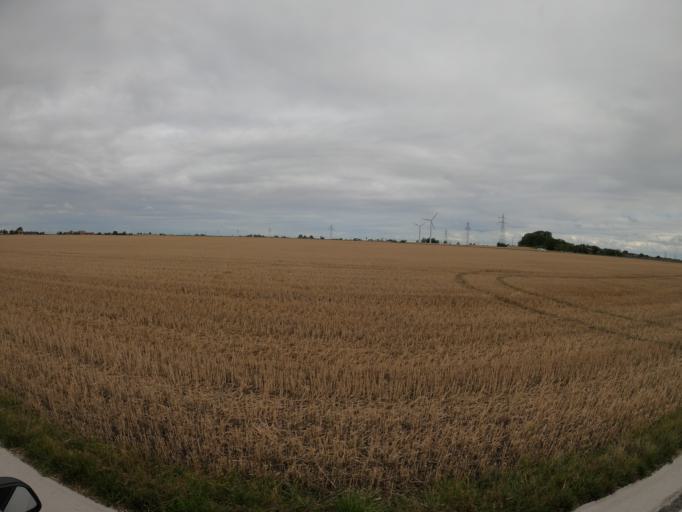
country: SE
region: Skane
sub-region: Kavlinge Kommun
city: Kaevlinge
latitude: 55.7458
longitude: 13.1393
